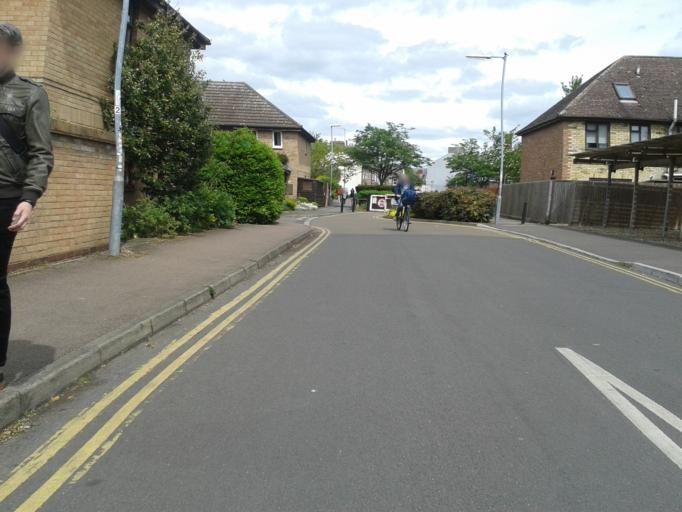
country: GB
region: England
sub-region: Cambridgeshire
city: Cambridge
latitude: 52.1954
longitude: 0.1421
